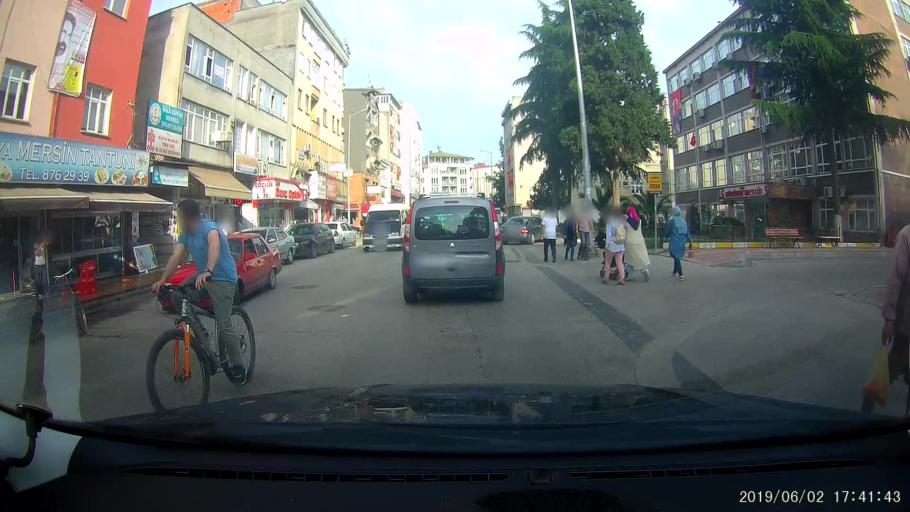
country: TR
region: Samsun
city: Terme
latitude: 41.2099
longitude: 36.9707
